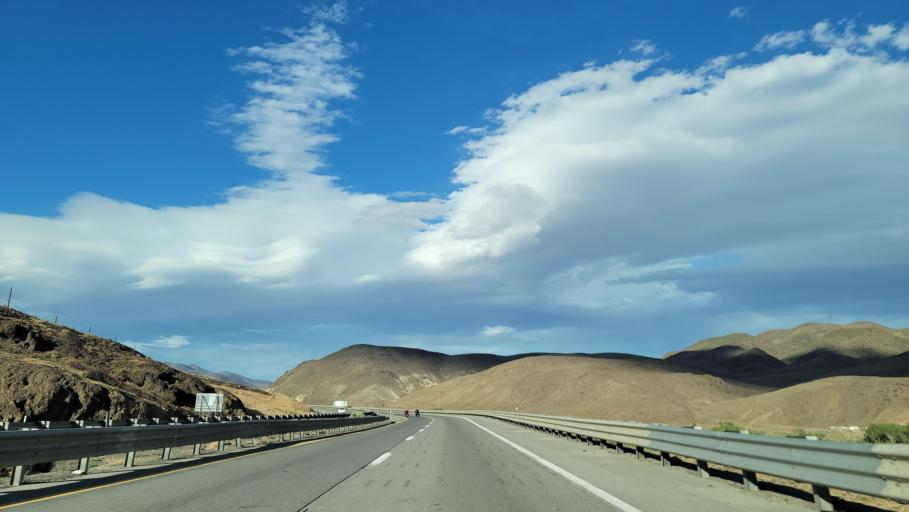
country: US
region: Nevada
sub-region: Washoe County
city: Sparks
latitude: 39.5322
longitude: -119.6110
